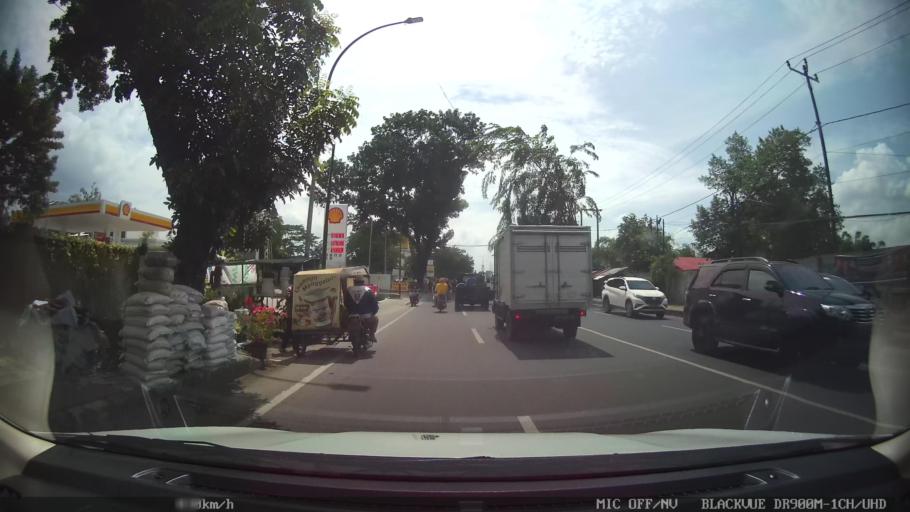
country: ID
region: North Sumatra
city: Medan
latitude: 3.6068
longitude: 98.6721
